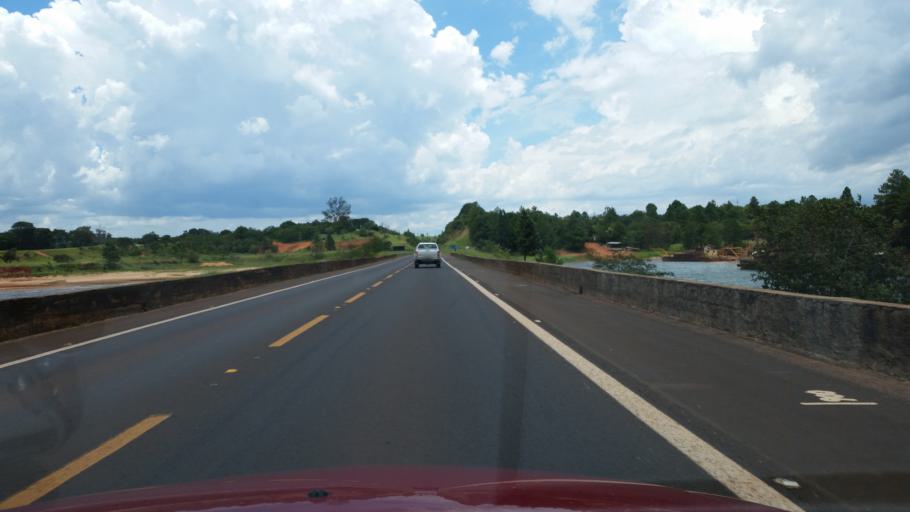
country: BR
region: Sao Paulo
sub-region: Itai
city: Itai
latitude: -23.2720
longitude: -49.0148
